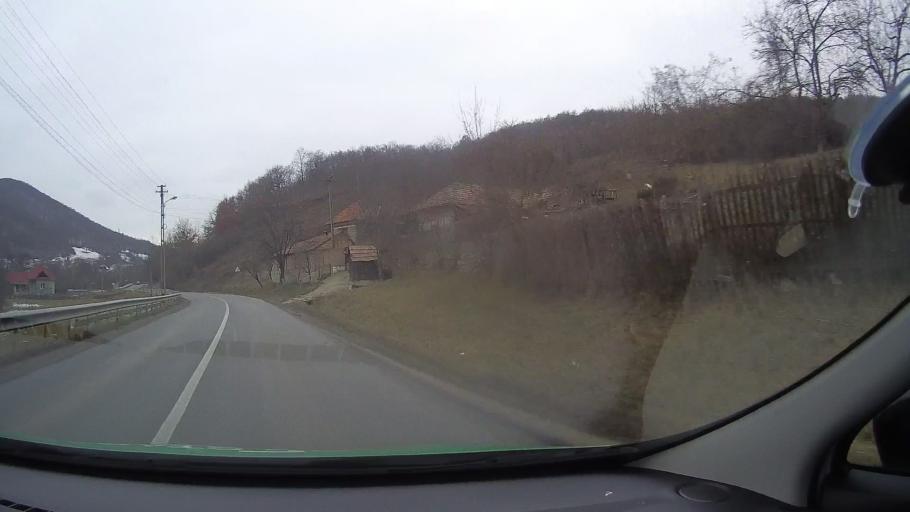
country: RO
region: Alba
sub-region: Comuna Metes
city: Metes
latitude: 46.1002
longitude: 23.4563
